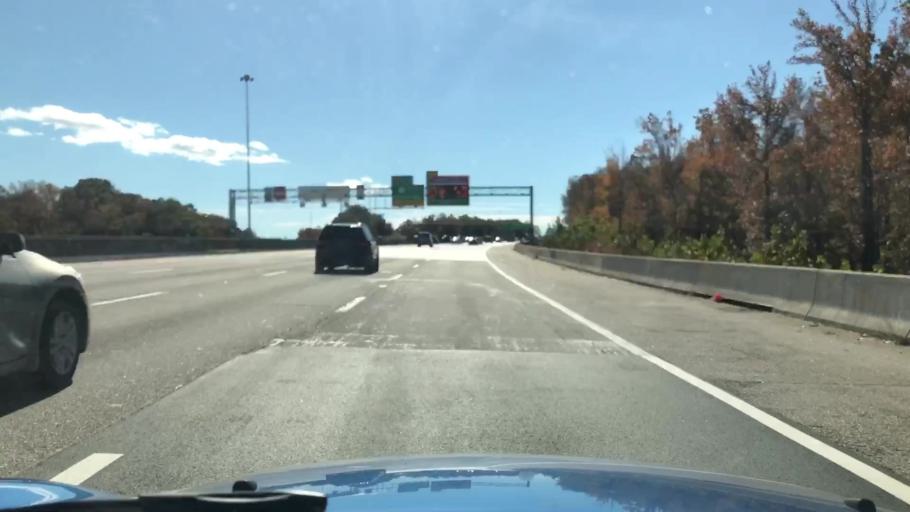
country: US
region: Virginia
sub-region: Fairfax County
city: Lorton
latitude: 38.6855
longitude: -77.2285
